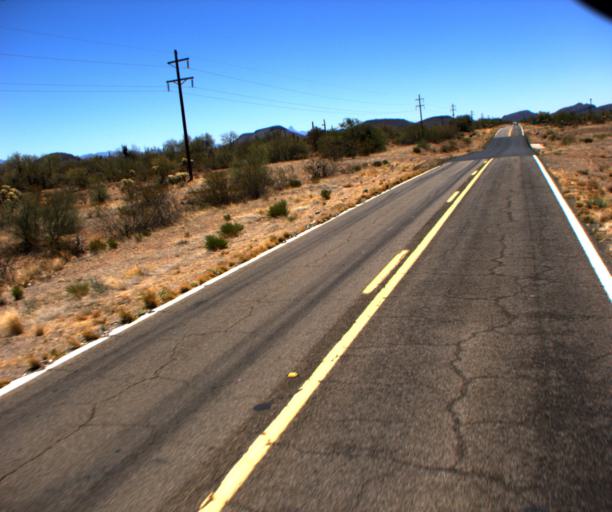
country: US
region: Arizona
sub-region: Pima County
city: Sells
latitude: 32.0160
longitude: -111.9981
